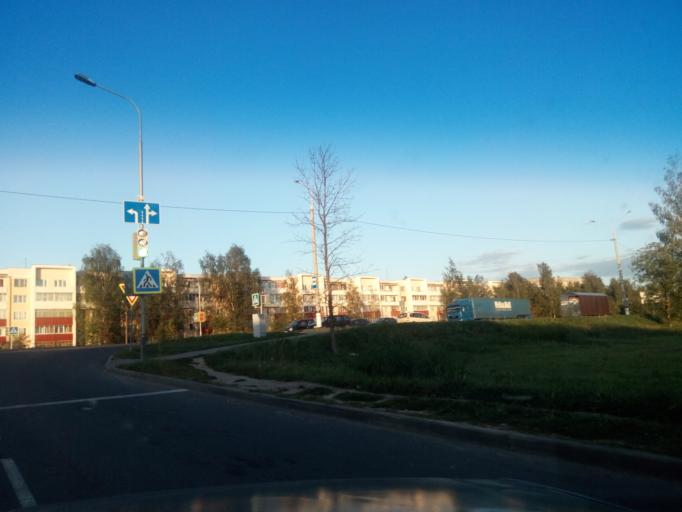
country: BY
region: Vitebsk
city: Polatsk
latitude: 55.4715
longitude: 28.7514
